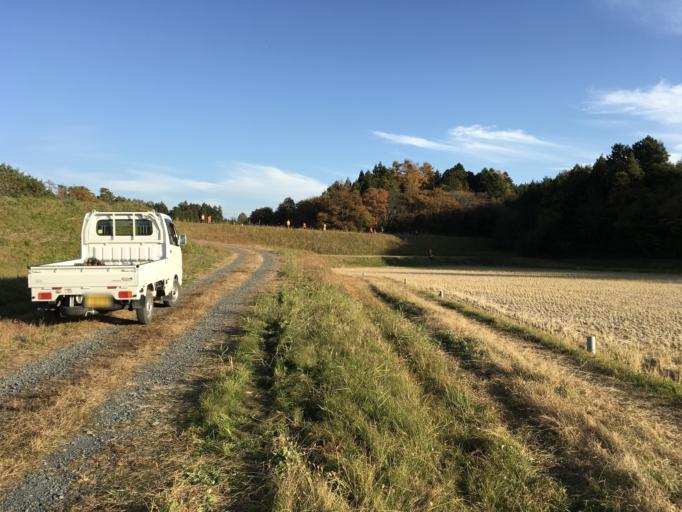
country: JP
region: Iwate
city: Ichinoseki
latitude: 38.7958
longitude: 141.1868
